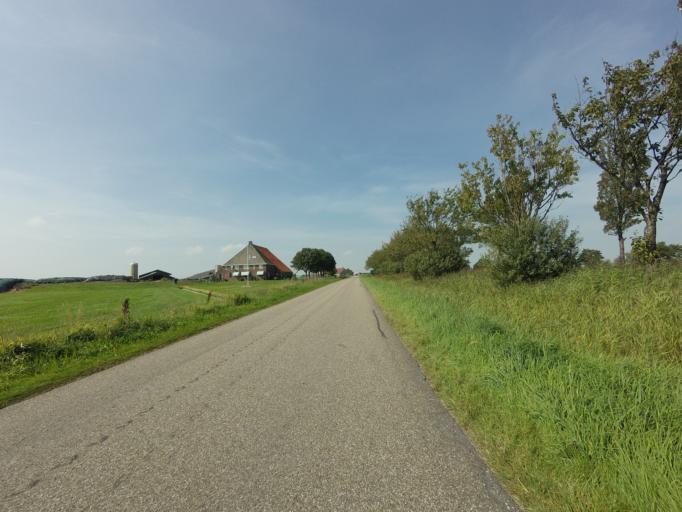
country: NL
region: Friesland
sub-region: Sudwest Fryslan
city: Woudsend
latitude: 52.9329
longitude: 5.6636
